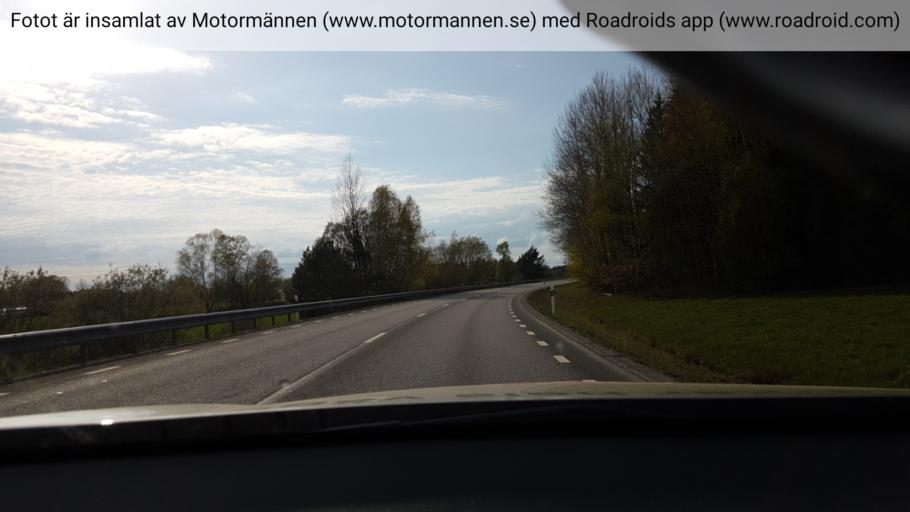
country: SE
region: Stockholm
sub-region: Nynashamns Kommun
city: Osmo
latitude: 58.9838
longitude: 17.8569
